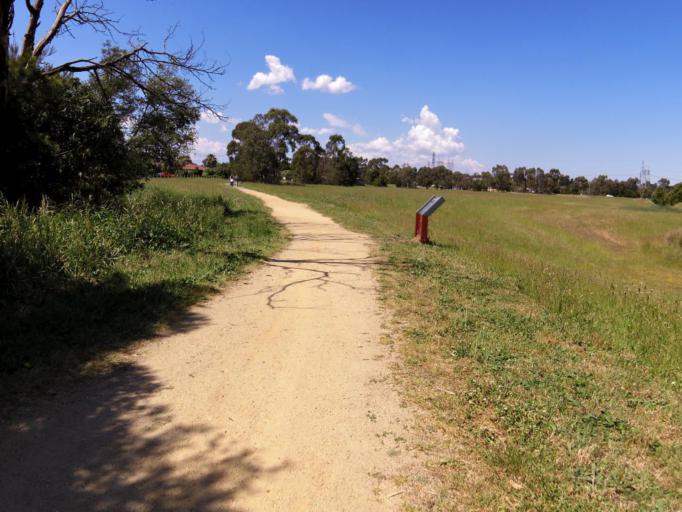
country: AU
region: Victoria
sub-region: Casey
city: Narre Warren South
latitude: -38.0364
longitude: 145.2762
